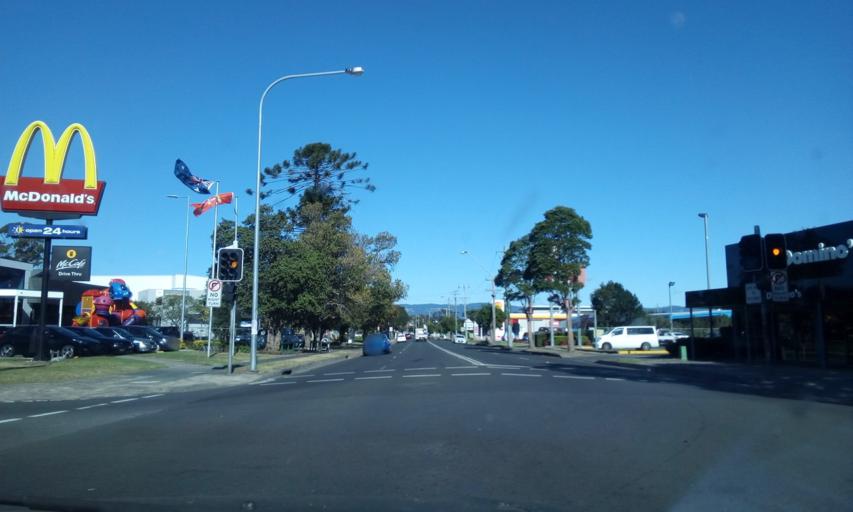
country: AU
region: New South Wales
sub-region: Wollongong
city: Dapto
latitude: -34.4952
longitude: 150.7934
